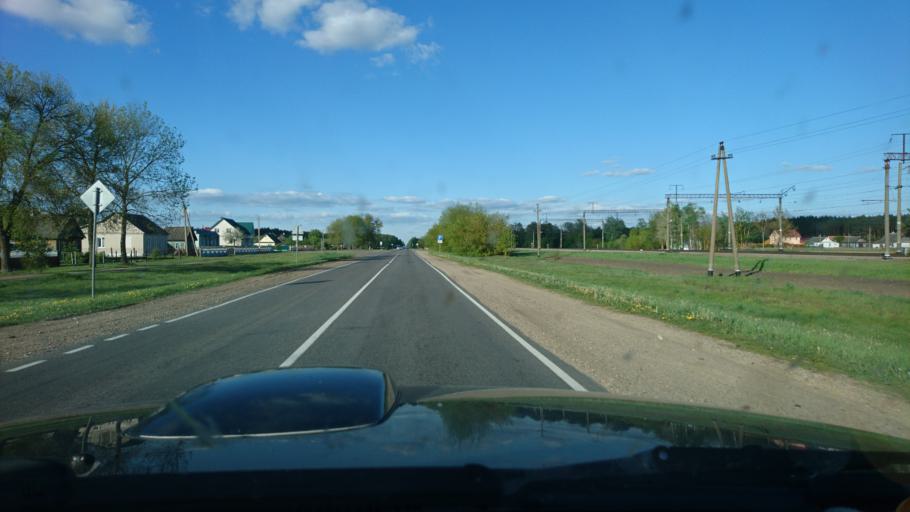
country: BY
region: Brest
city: Nyakhachava
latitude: 52.6487
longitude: 25.2152
